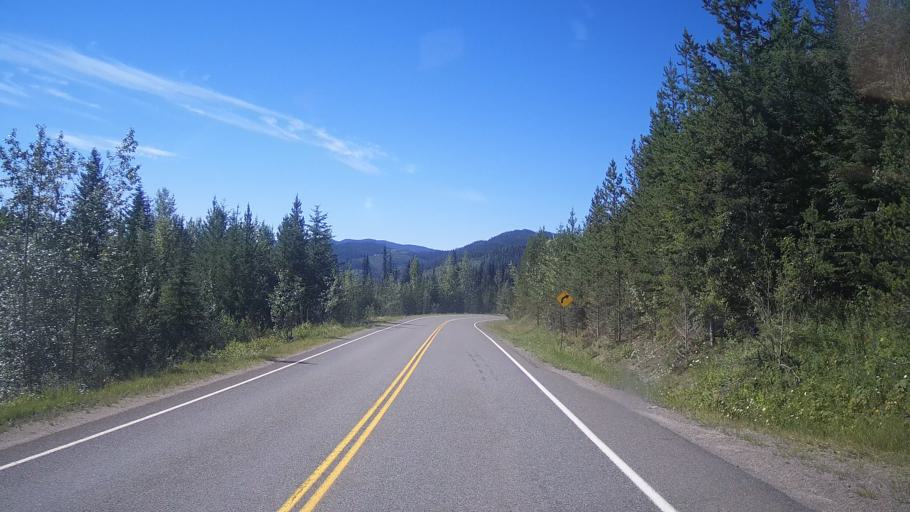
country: CA
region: British Columbia
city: Kamloops
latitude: 51.4824
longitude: -120.4678
